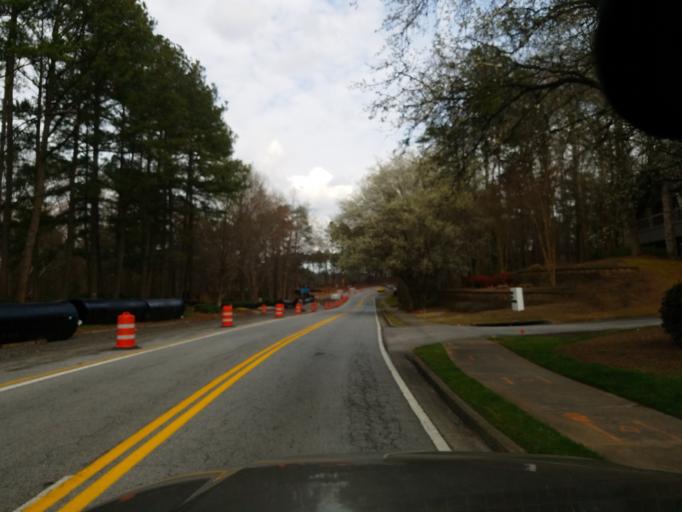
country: US
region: Georgia
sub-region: Cobb County
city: Smyrna
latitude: 33.9093
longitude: -84.4825
